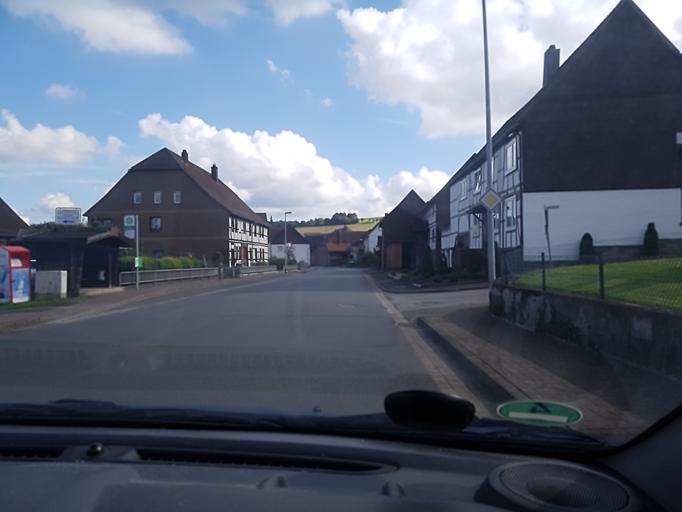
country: DE
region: Lower Saxony
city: Uslar
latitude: 51.6703
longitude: 9.5972
